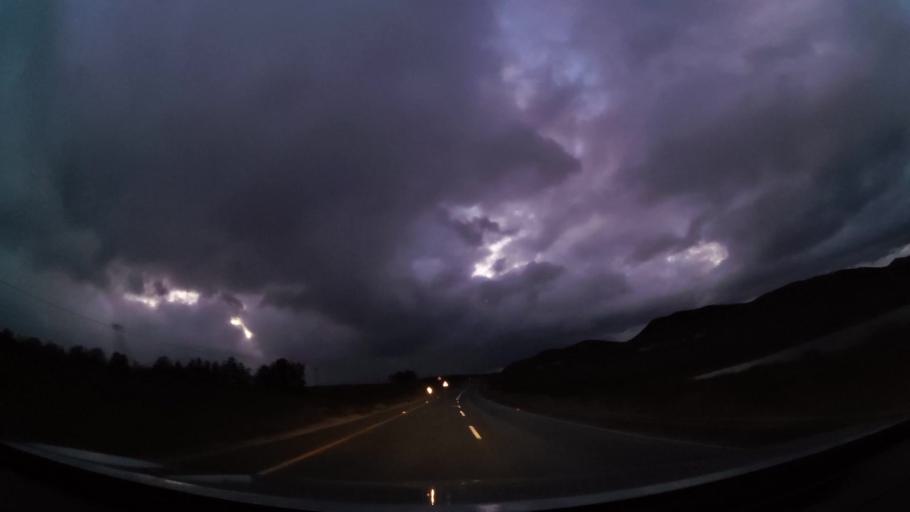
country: ZA
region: Western Cape
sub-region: Overberg District Municipality
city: Swellendam
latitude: -33.9025
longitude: 20.3925
